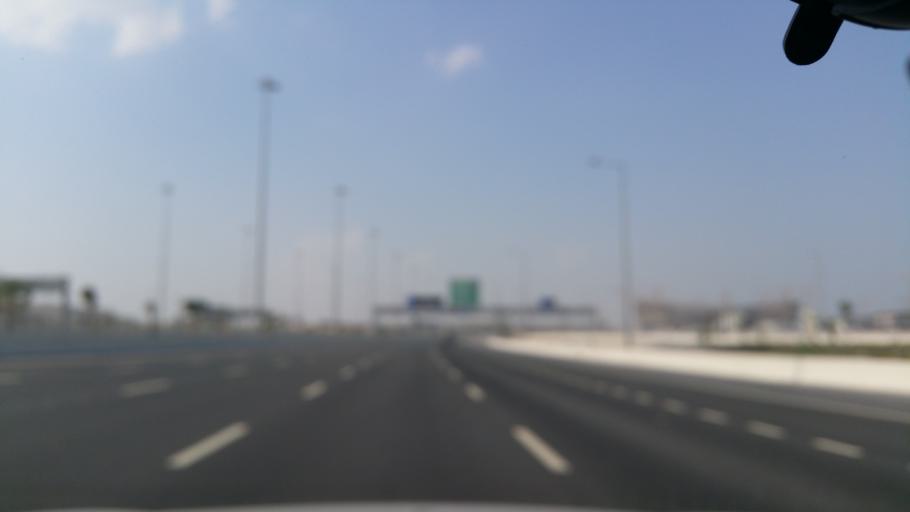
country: QA
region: Baladiyat Umm Salal
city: Umm Salal Muhammad
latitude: 25.4058
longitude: 51.4909
